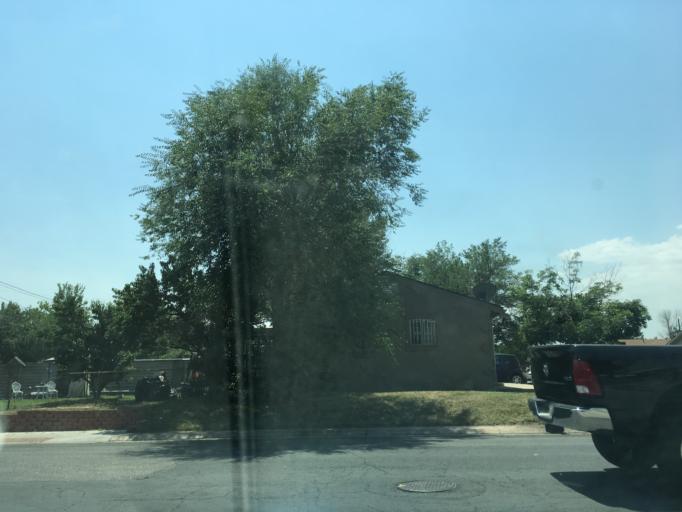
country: US
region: Colorado
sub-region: Jefferson County
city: Lakewood
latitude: 39.6968
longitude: -105.0319
